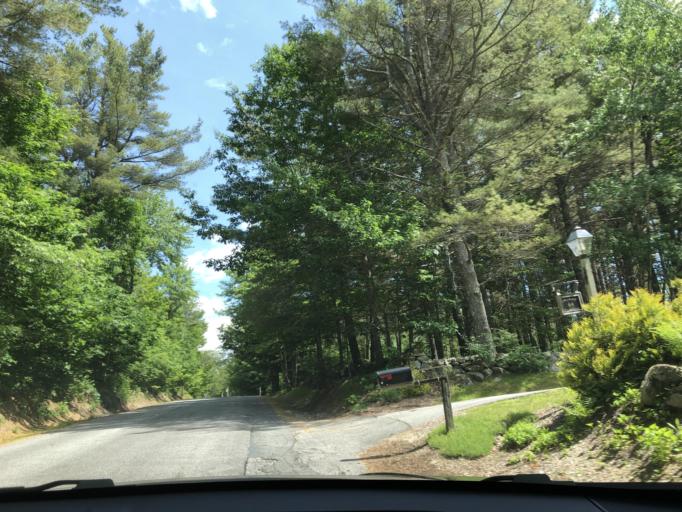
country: US
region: New Hampshire
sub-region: Merrimack County
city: New London
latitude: 43.4124
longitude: -72.0062
